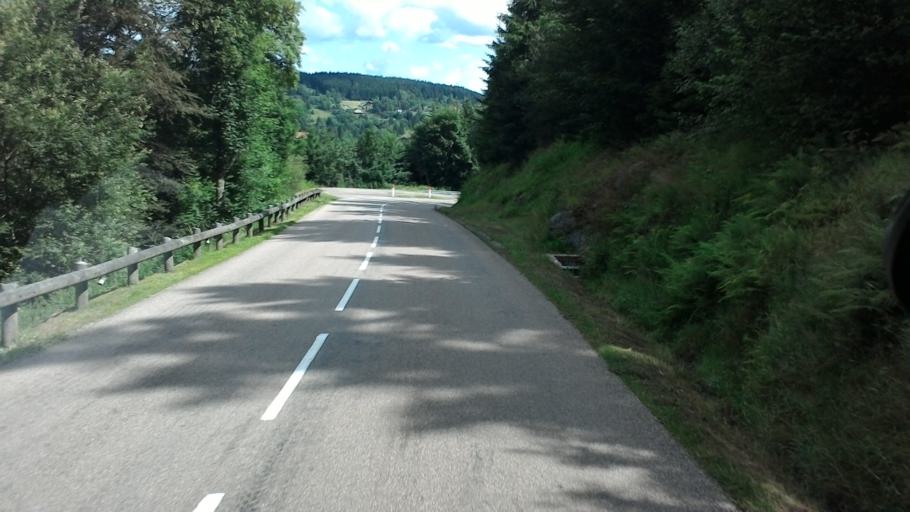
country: FR
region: Lorraine
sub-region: Departement des Vosges
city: Gerardmer
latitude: 48.0398
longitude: 6.8648
